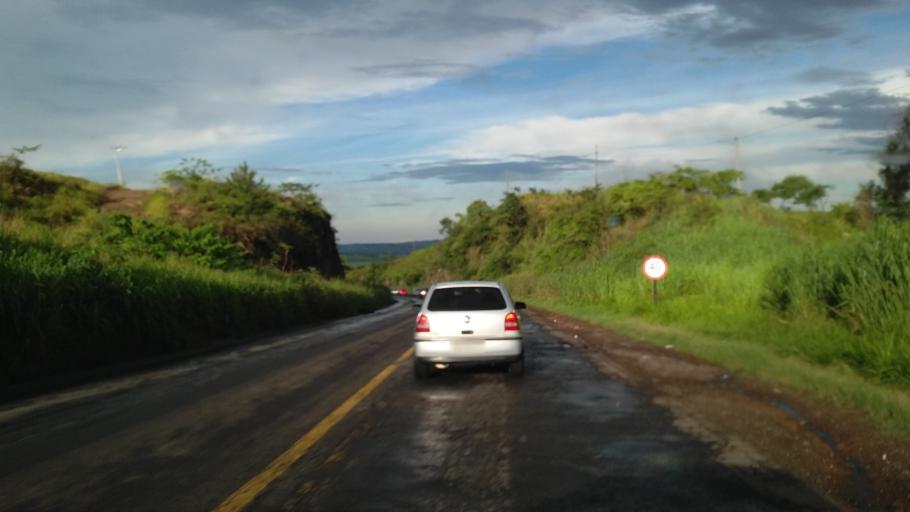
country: BR
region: Sao Paulo
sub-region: Marilia
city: Marilia
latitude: -22.1268
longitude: -49.9355
